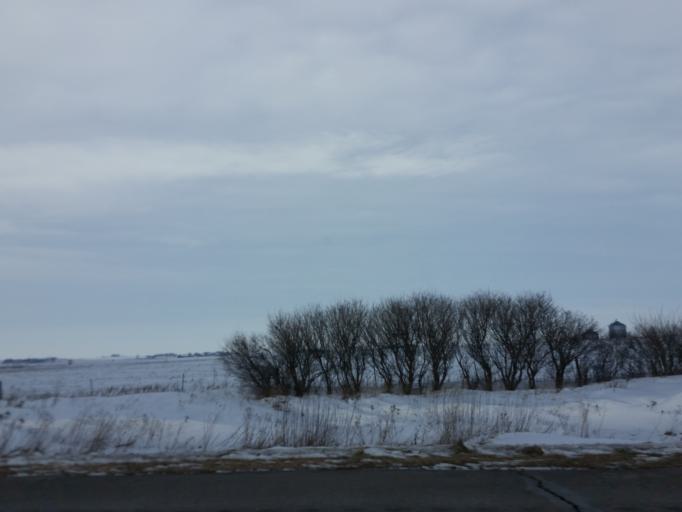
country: US
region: Iowa
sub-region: Delaware County
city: Manchester
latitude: 42.4646
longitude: -91.6065
